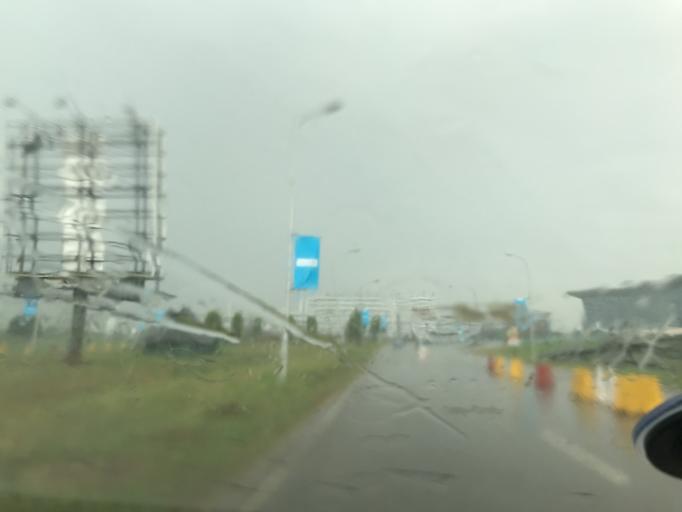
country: NG
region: Lagos
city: Oshodi
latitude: 6.5739
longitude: 3.3214
